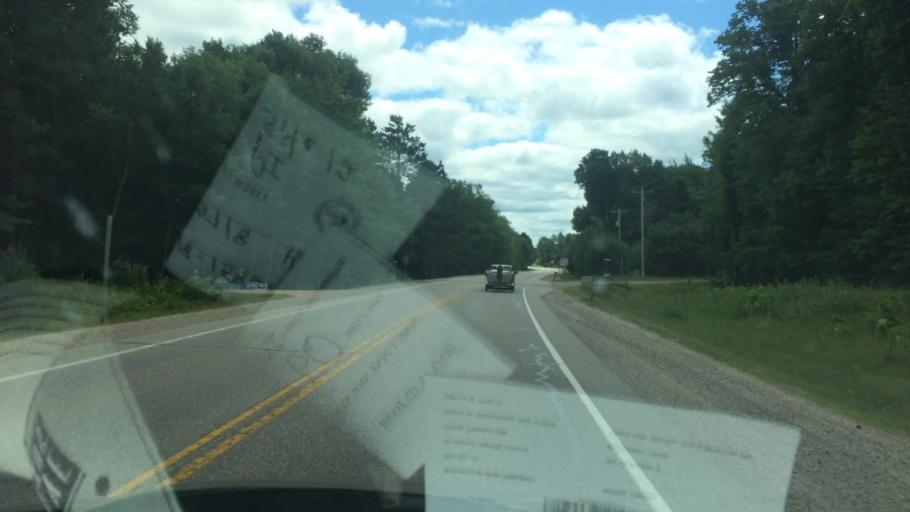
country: US
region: Wisconsin
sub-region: Vilas County
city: Eagle River
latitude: 45.8053
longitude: -89.3198
